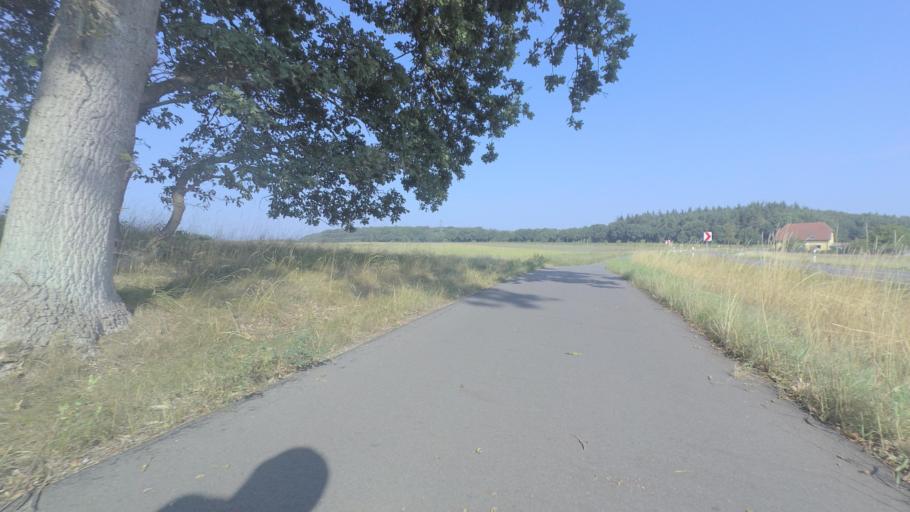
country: DE
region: Mecklenburg-Vorpommern
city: Malchow
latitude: 53.4976
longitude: 12.4229
